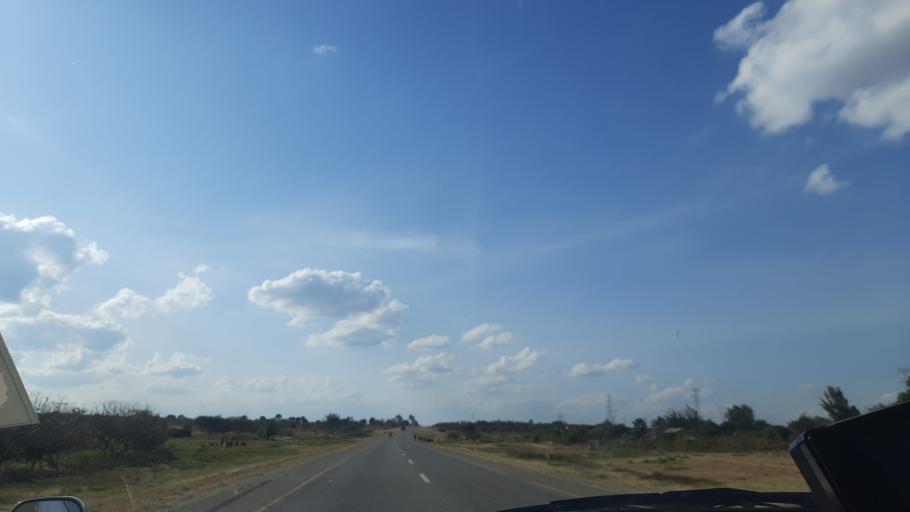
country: TZ
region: Singida
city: Puma
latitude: -5.0392
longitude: 34.7595
